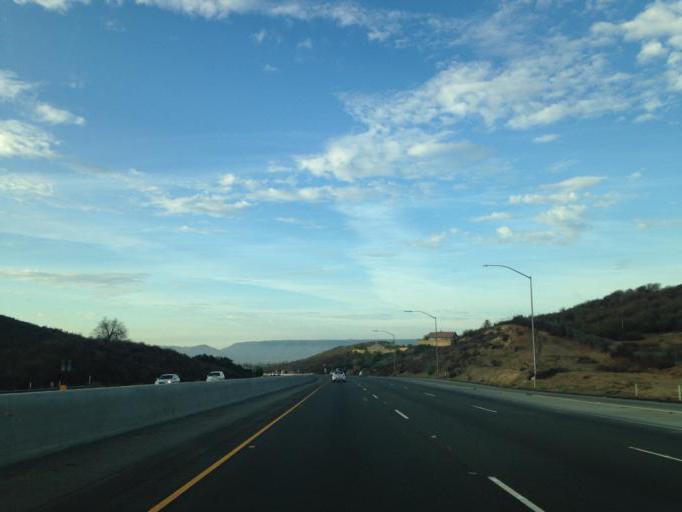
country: US
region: California
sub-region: Riverside County
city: Murrieta Hot Springs
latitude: 33.5953
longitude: -117.1771
